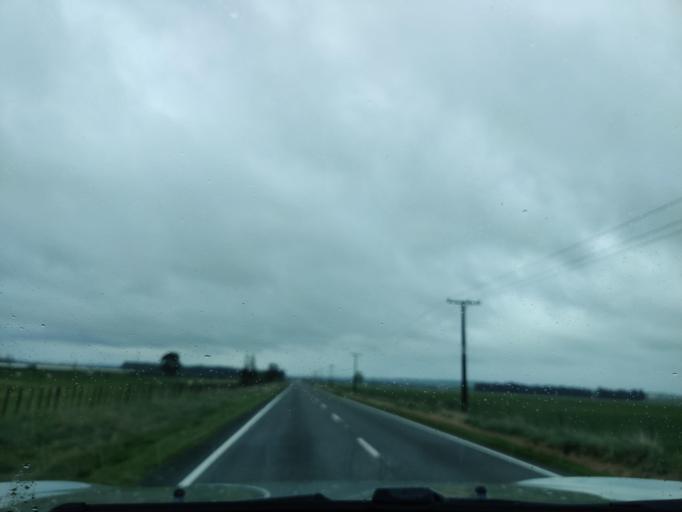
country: NZ
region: Hawke's Bay
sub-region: Hastings District
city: Hastings
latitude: -40.0122
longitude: 176.3701
